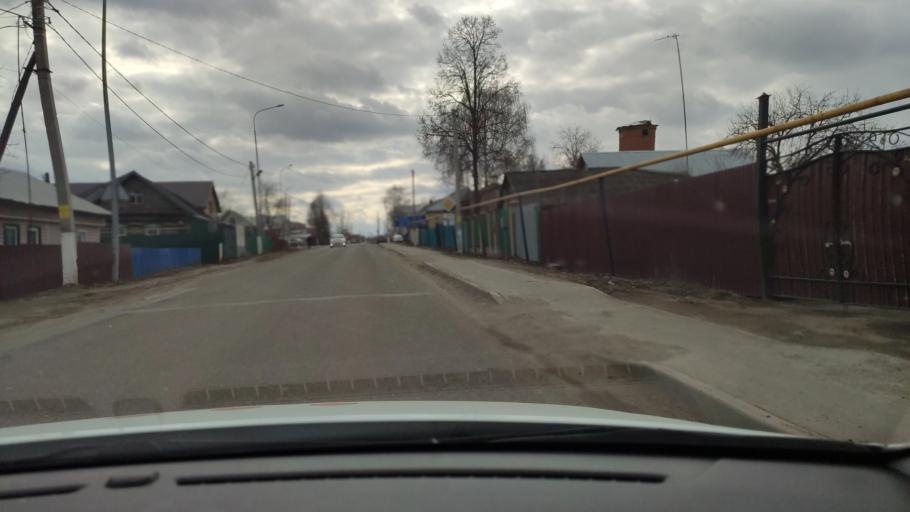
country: RU
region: Tatarstan
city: Vysokaya Gora
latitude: 56.1228
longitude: 49.1974
